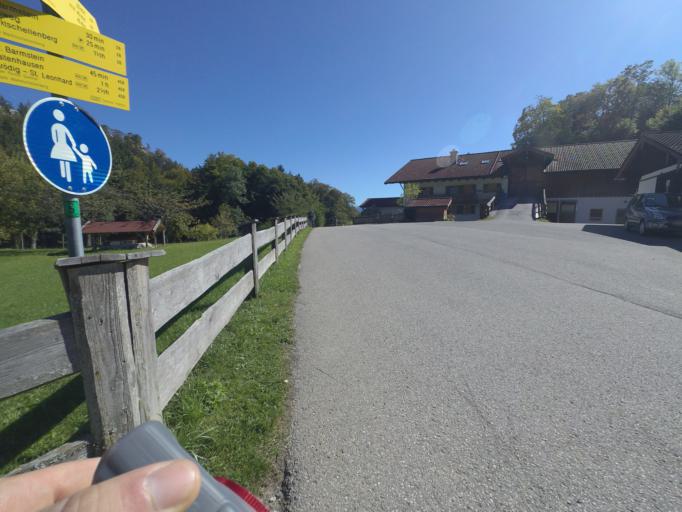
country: AT
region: Salzburg
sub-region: Politischer Bezirk Hallein
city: Hallein
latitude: 47.6870
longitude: 13.0768
